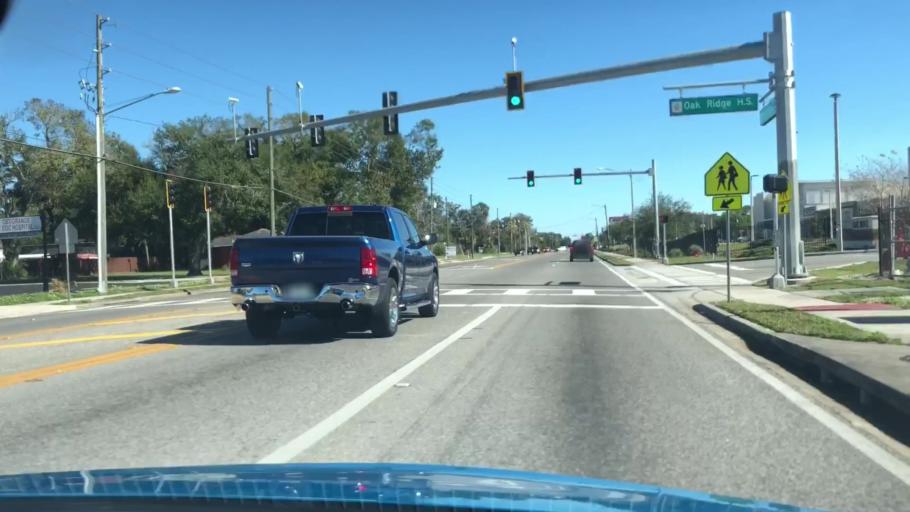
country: US
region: Florida
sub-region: Orange County
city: Sky Lake
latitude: 28.4726
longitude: -81.3876
